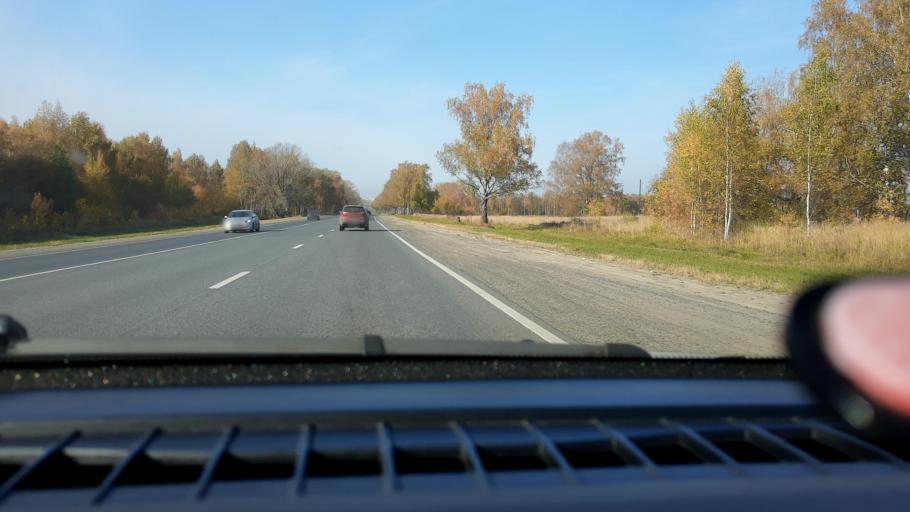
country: RU
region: Nizjnij Novgorod
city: Kstovo
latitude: 56.1335
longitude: 44.2459
